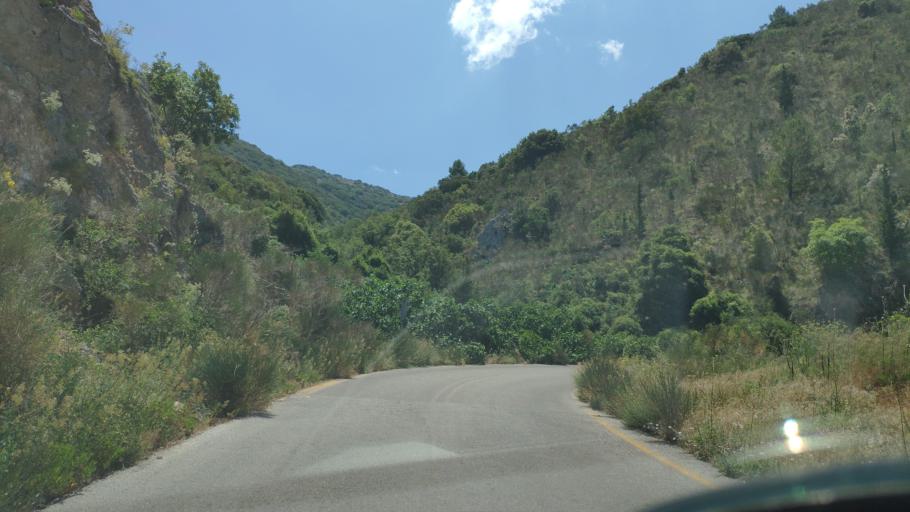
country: GR
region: Ionian Islands
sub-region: Lefkada
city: Nidri
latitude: 38.7440
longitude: 20.6217
